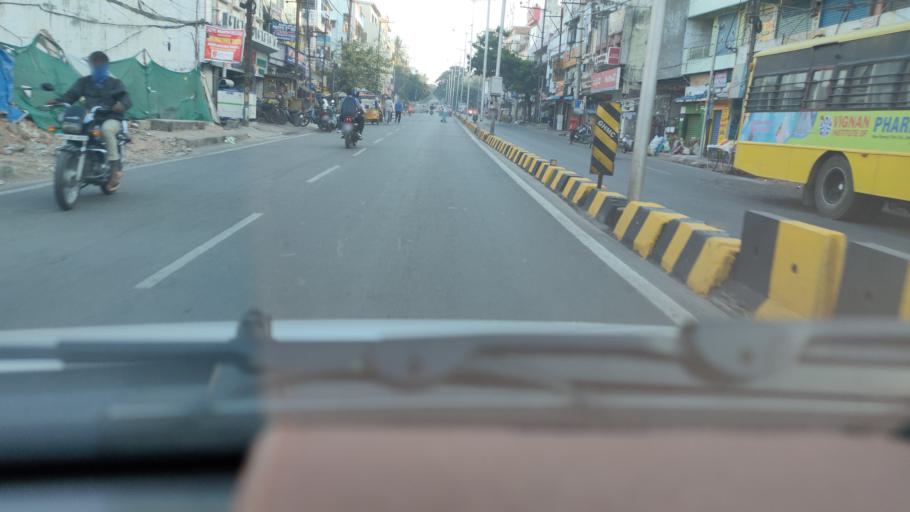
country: IN
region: Telangana
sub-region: Rangareddi
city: Gaddi Annaram
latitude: 17.3989
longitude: 78.5127
